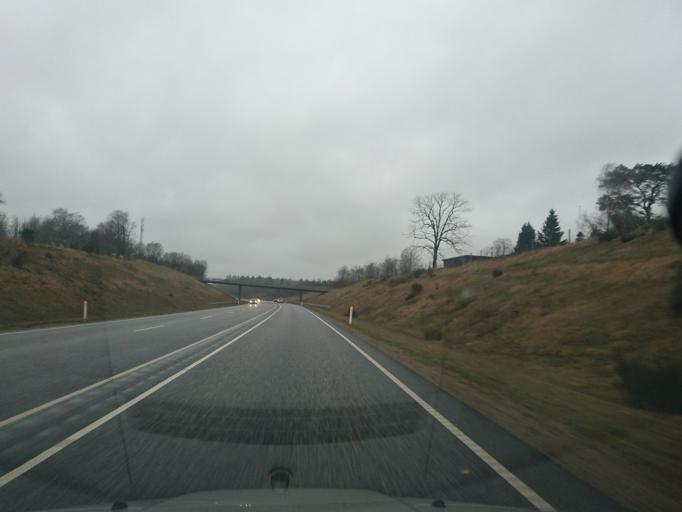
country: DK
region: South Denmark
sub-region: Vejle Kommune
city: Egtved
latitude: 55.7047
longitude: 9.2878
